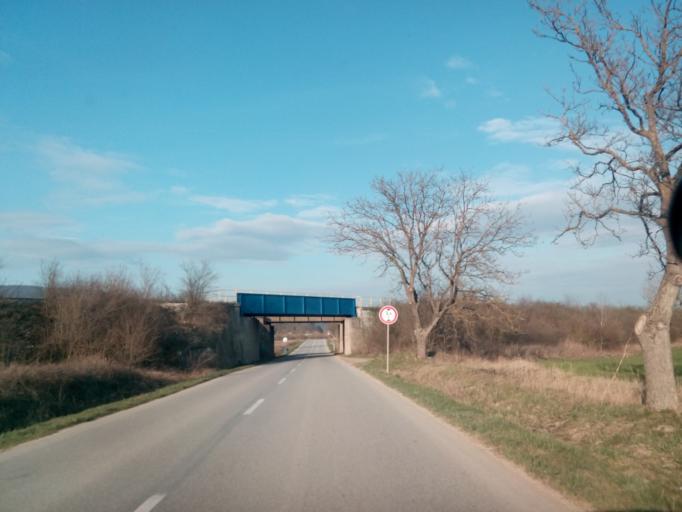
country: SK
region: Kosicky
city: Medzev
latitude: 48.5933
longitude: 20.8643
